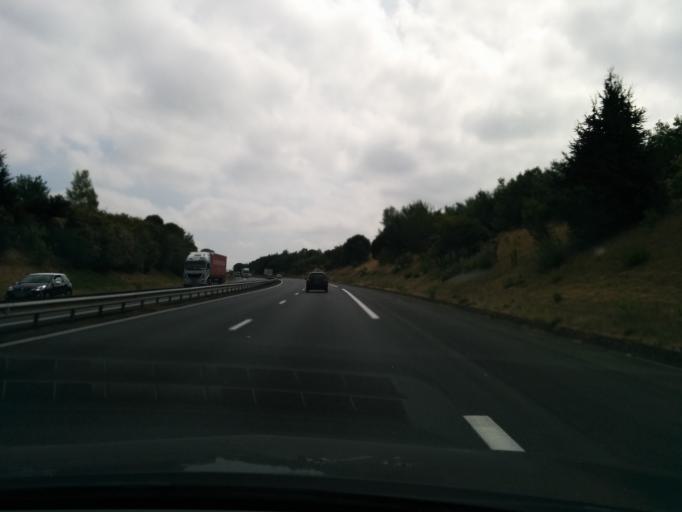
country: FR
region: Midi-Pyrenees
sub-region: Departement de la Haute-Garonne
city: Rouffiac-Tolosan
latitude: 43.6548
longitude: 1.5370
